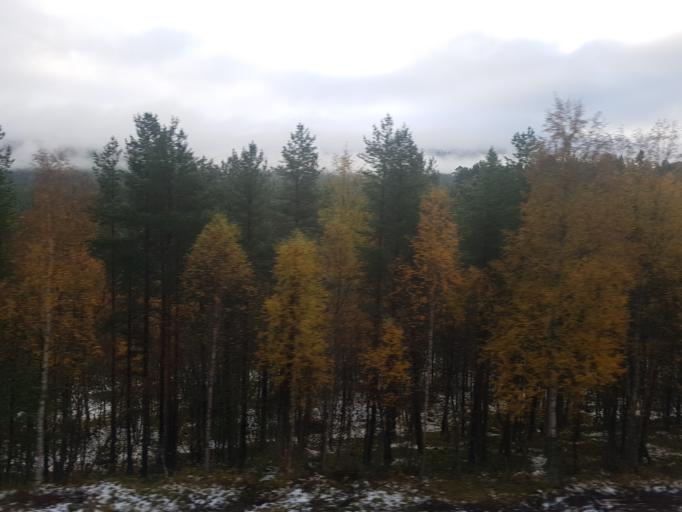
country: NO
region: Sor-Trondelag
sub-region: Oppdal
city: Oppdal
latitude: 62.6458
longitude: 9.8319
